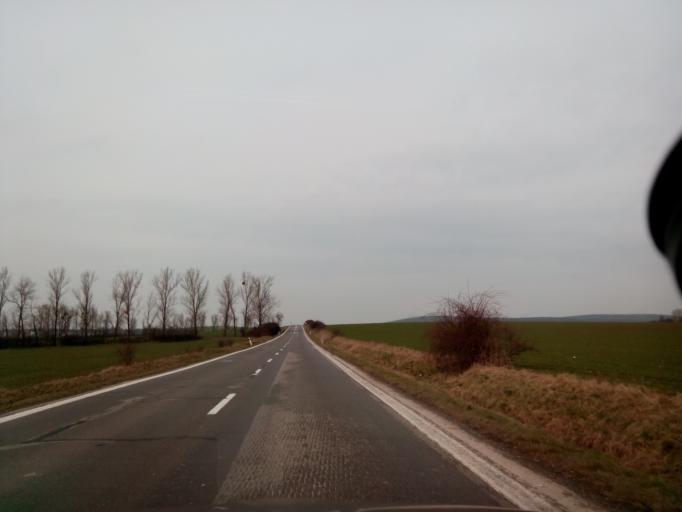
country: HU
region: Borsod-Abauj-Zemplen
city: Satoraljaujhely
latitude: 48.4734
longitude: 21.6411
